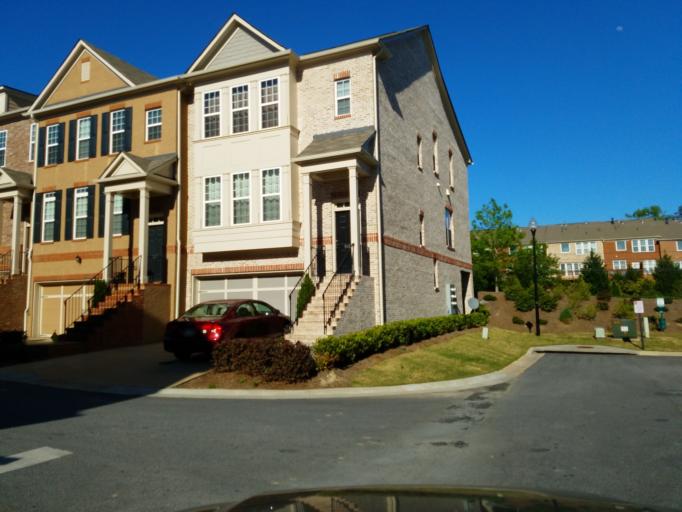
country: US
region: Georgia
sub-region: Cobb County
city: Vinings
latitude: 33.8323
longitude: -84.4829
